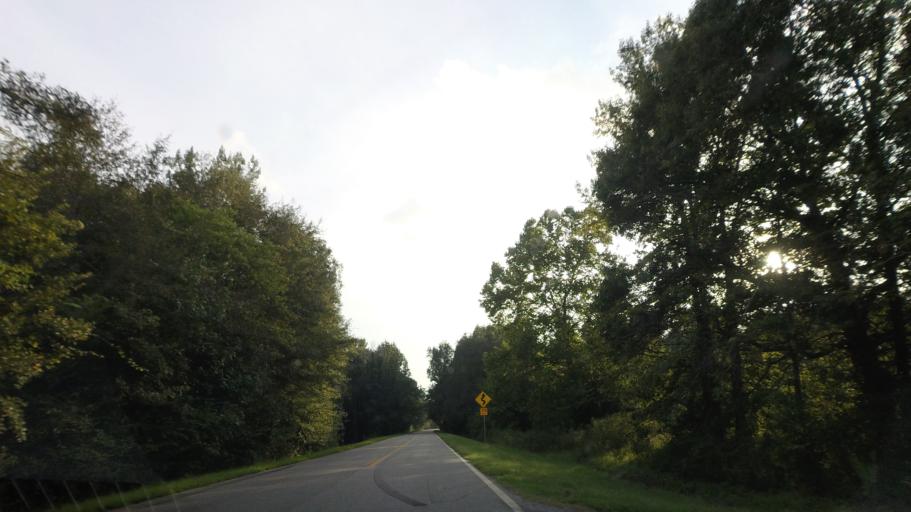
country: US
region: Georgia
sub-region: Wilkinson County
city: Gordon
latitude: 32.8273
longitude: -83.3881
